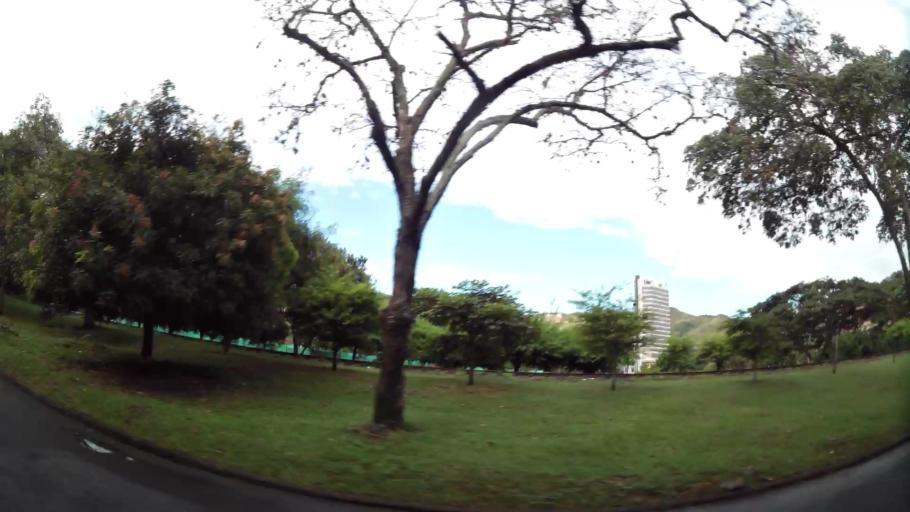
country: CO
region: Valle del Cauca
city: Cali
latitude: 3.4732
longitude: -76.5240
